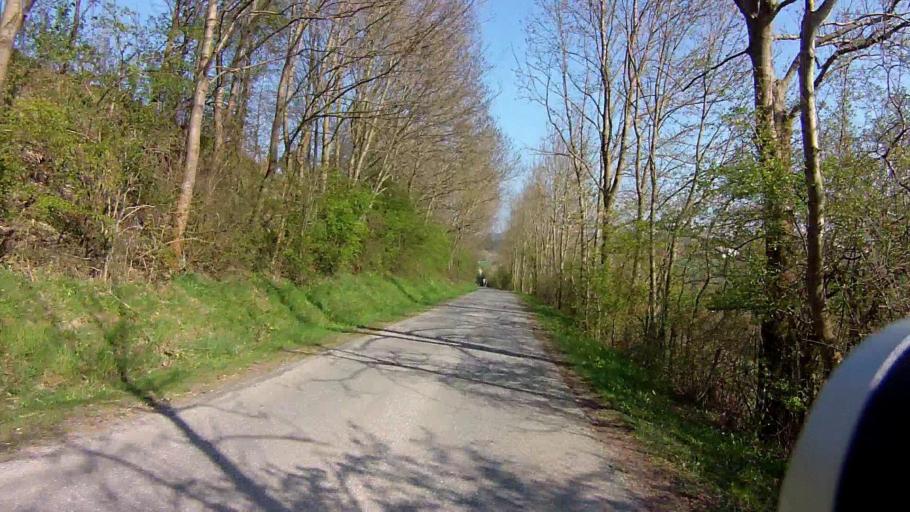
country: DE
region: North Rhine-Westphalia
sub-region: Regierungsbezirk Detmold
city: Paderborn
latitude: 51.6980
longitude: 8.8204
